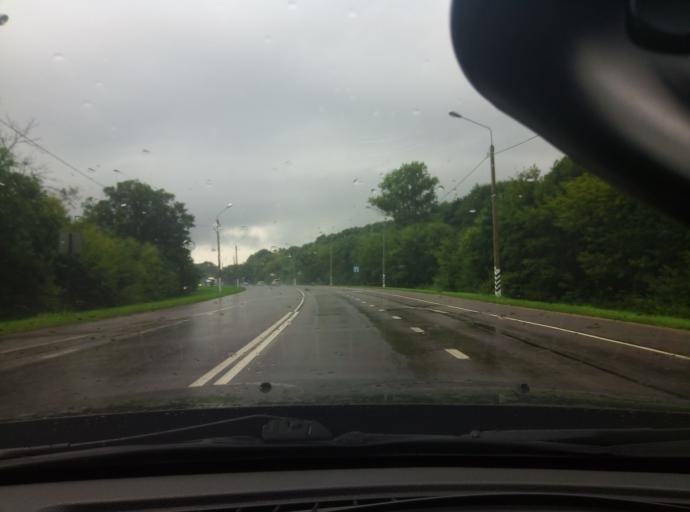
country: RU
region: Tula
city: Shchekino
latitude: 53.9012
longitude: 37.4601
